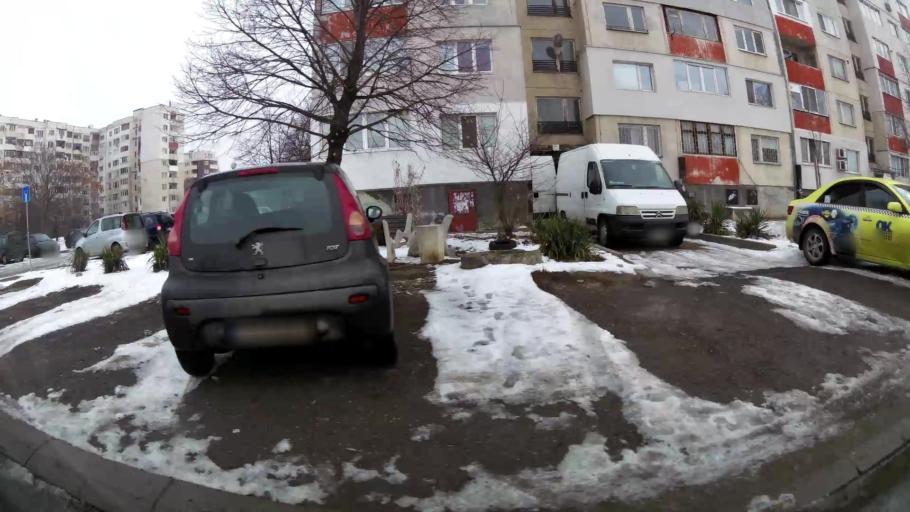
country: BG
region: Sofia-Capital
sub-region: Stolichna Obshtina
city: Sofia
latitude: 42.7115
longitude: 23.3757
